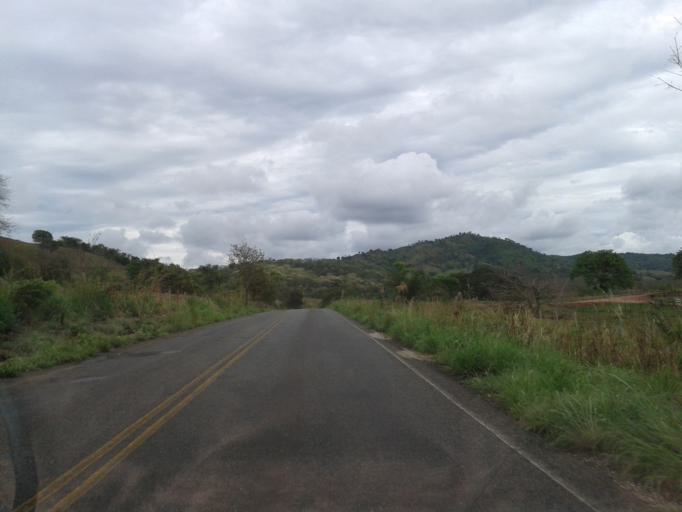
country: BR
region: Goias
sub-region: Caldas Novas
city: Caldas Novas
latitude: -18.0584
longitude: -48.7043
